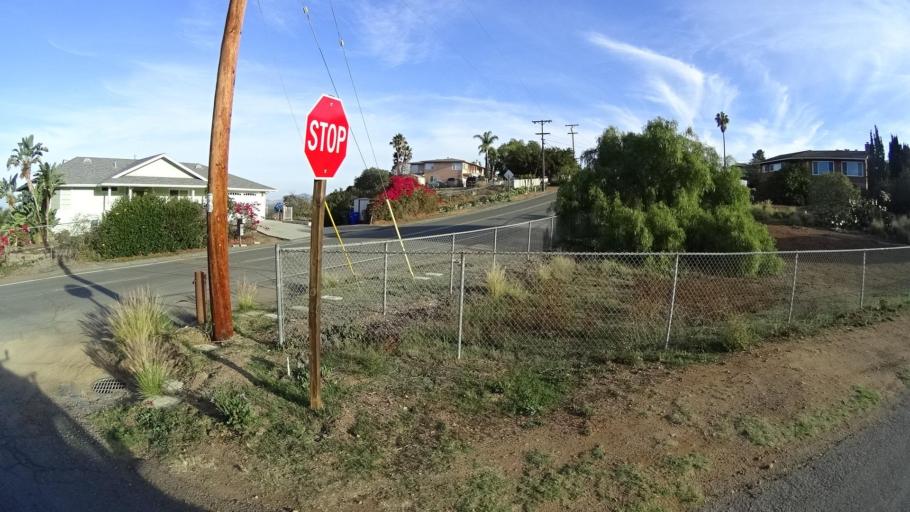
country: US
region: California
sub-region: San Diego County
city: Spring Valley
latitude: 32.7294
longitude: -116.9966
